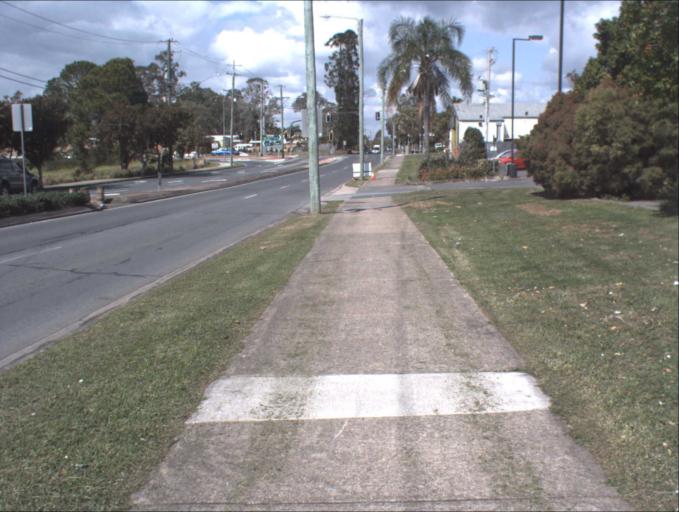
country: AU
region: Queensland
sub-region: Logan
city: Waterford West
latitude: -27.6907
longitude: 153.1363
